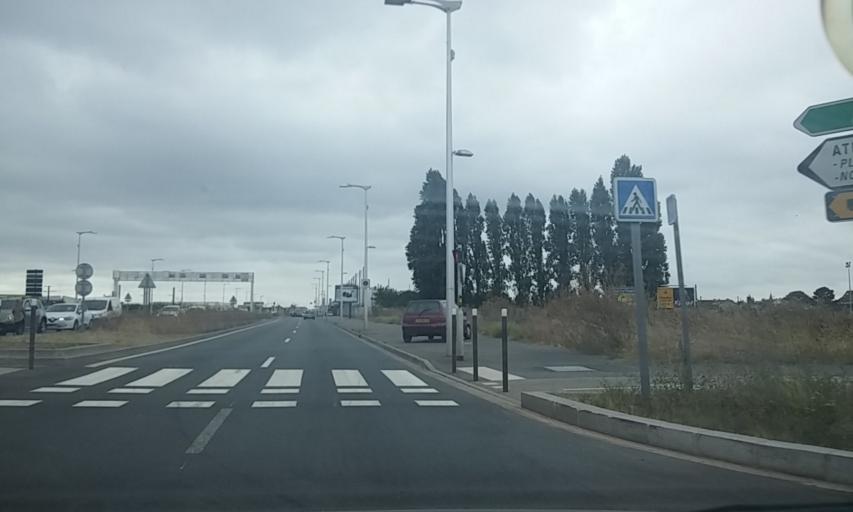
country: FR
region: Ile-de-France
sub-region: Departement de l'Essonne
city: Paray-Vieille-Poste
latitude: 48.7162
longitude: 2.3708
